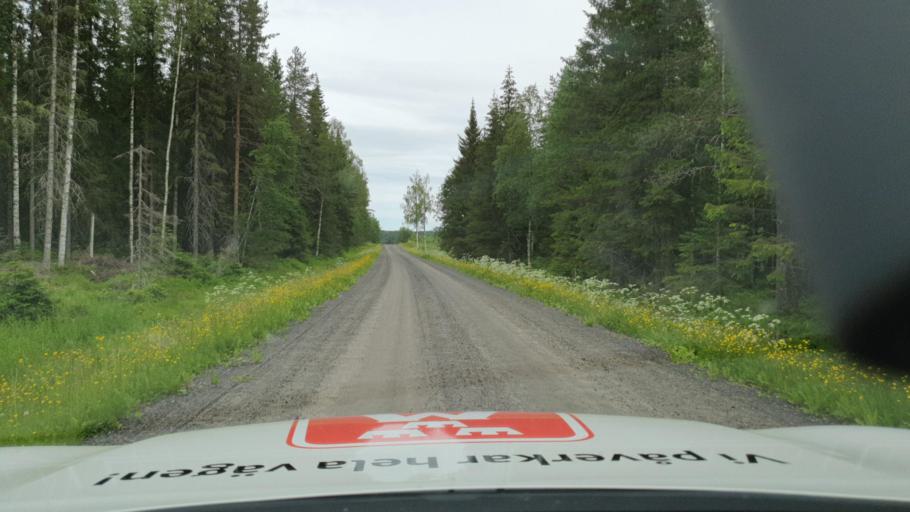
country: SE
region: Vaesterbotten
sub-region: Skelleftea Kommun
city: Burtraesk
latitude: 64.3845
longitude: 20.6140
